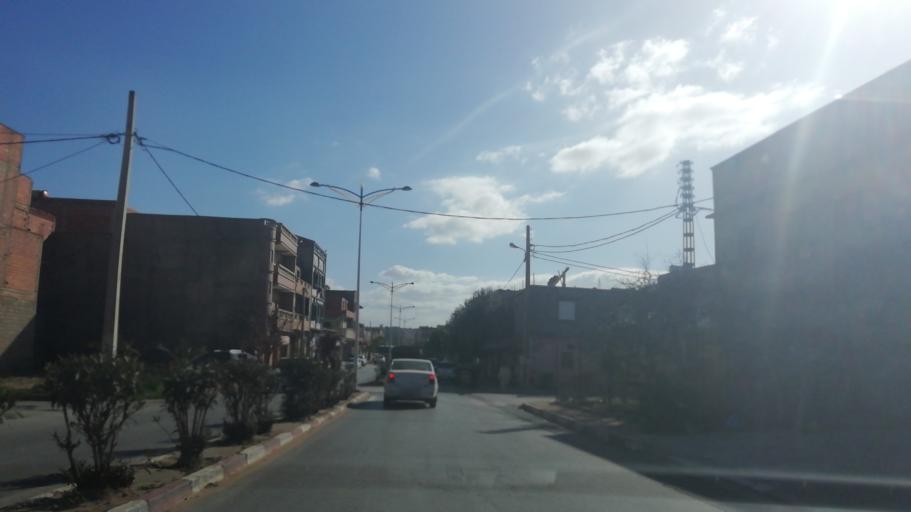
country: DZ
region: Mostaganem
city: Mostaganem
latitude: 35.9989
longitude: 0.3048
